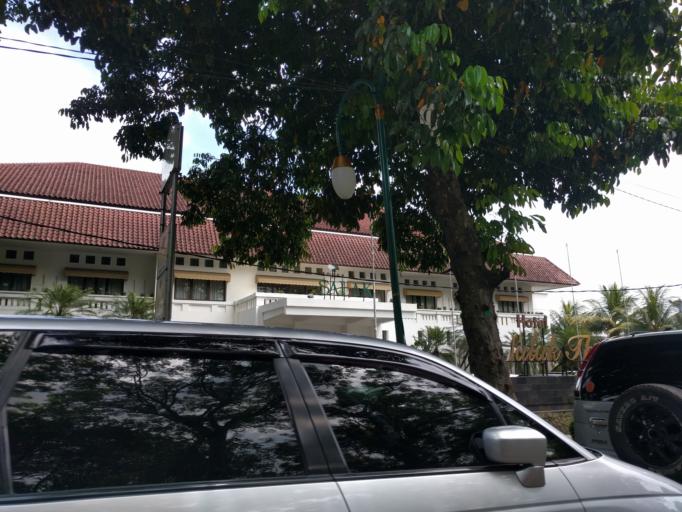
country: ID
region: West Java
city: Bogor
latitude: -6.5949
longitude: 106.7945
